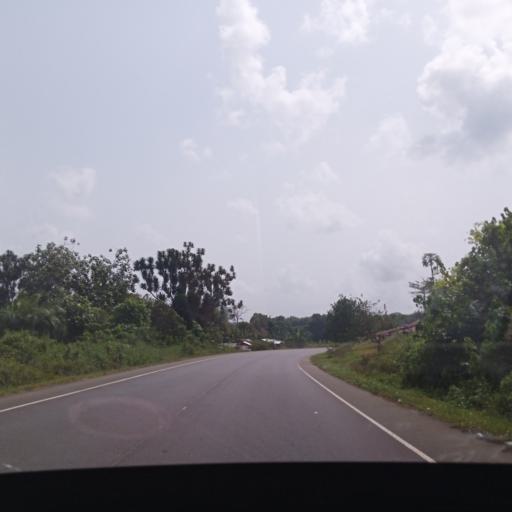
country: LR
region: Margibi
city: Kakata
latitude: 6.2314
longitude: -10.2795
